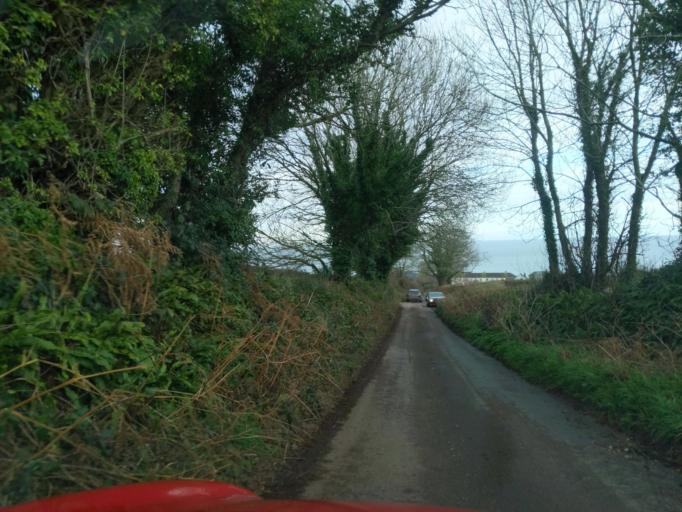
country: GB
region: England
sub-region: Devon
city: Salcombe
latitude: 50.2528
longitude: -3.6624
